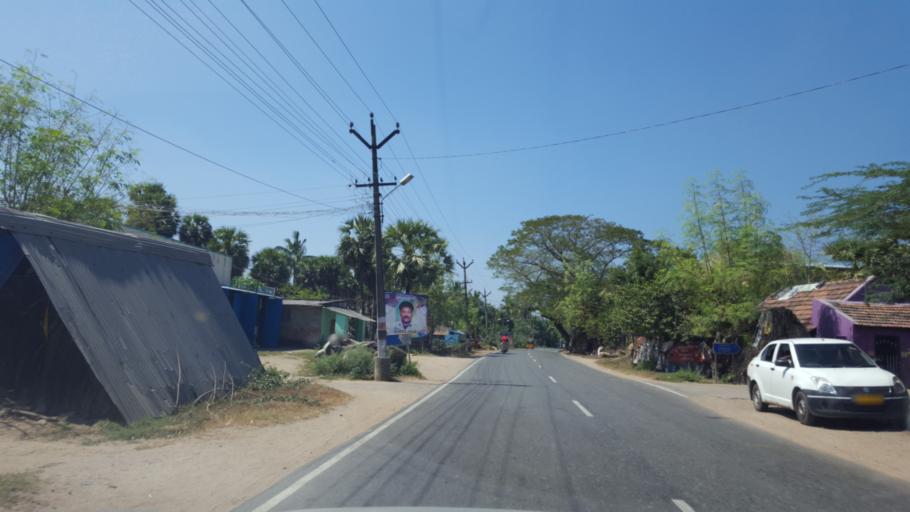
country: IN
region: Tamil Nadu
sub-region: Kancheepuram
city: Chengalpattu
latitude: 12.7283
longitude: 79.9494
